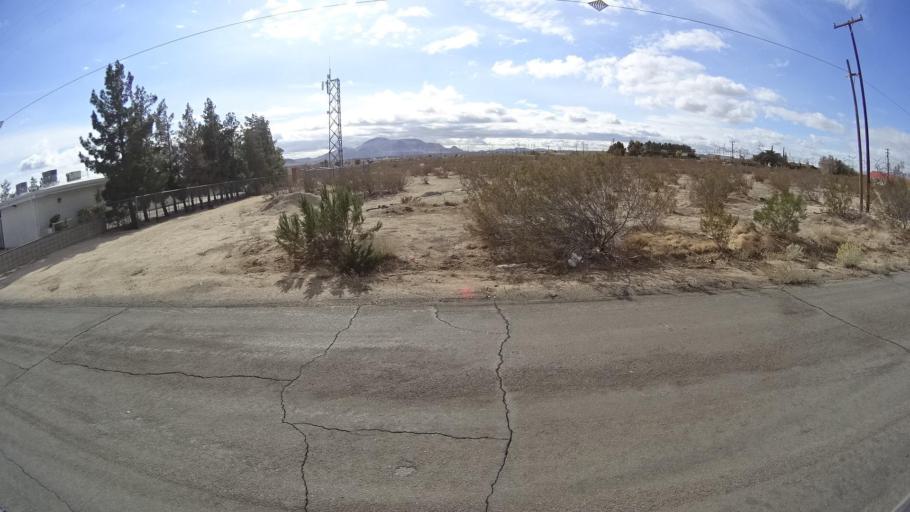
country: US
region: California
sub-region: Kern County
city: Mojave
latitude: 35.0613
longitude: -118.1928
